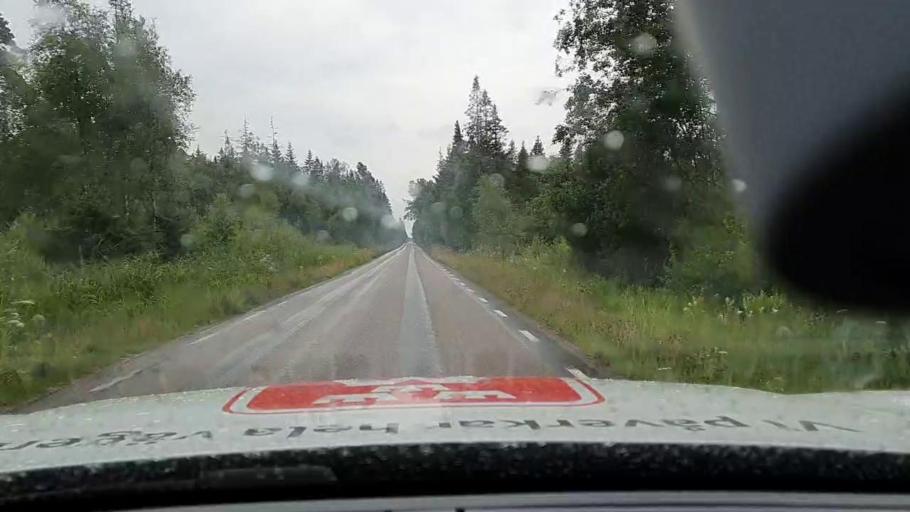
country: SE
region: Vaestra Goetaland
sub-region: Skovde Kommun
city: Skoevde
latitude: 58.4388
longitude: 13.7637
